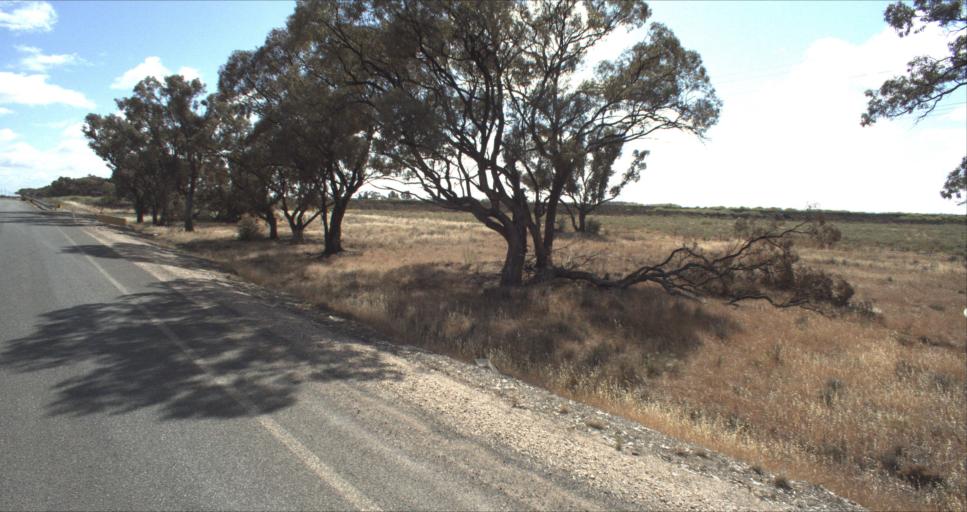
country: AU
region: New South Wales
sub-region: Murrumbidgee Shire
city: Darlington Point
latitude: -34.5545
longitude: 146.1701
